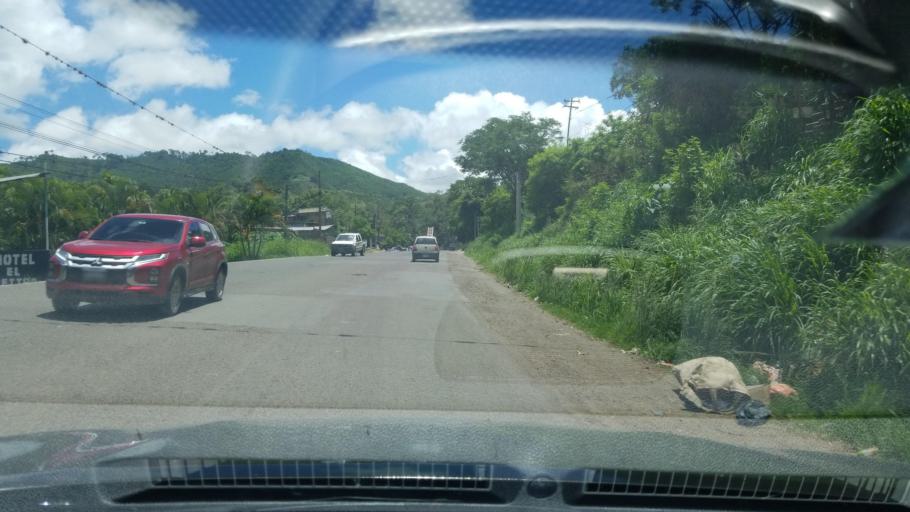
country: HN
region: Francisco Morazan
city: Rio Abajo
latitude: 14.1436
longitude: -87.2278
